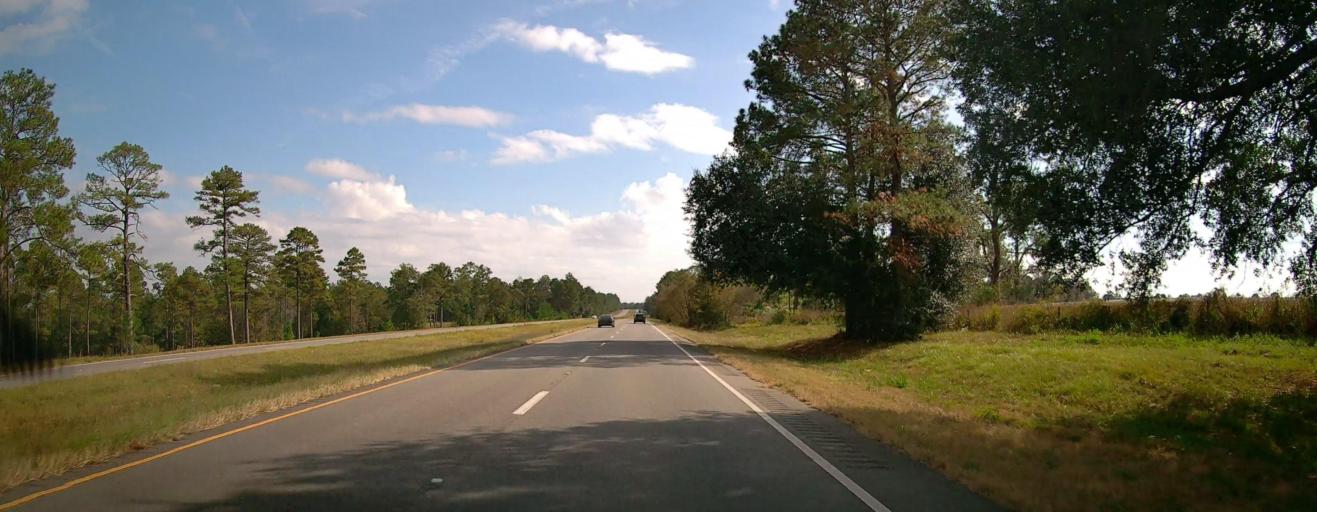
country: US
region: Georgia
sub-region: Thomas County
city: Meigs
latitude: 30.9627
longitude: -84.0304
